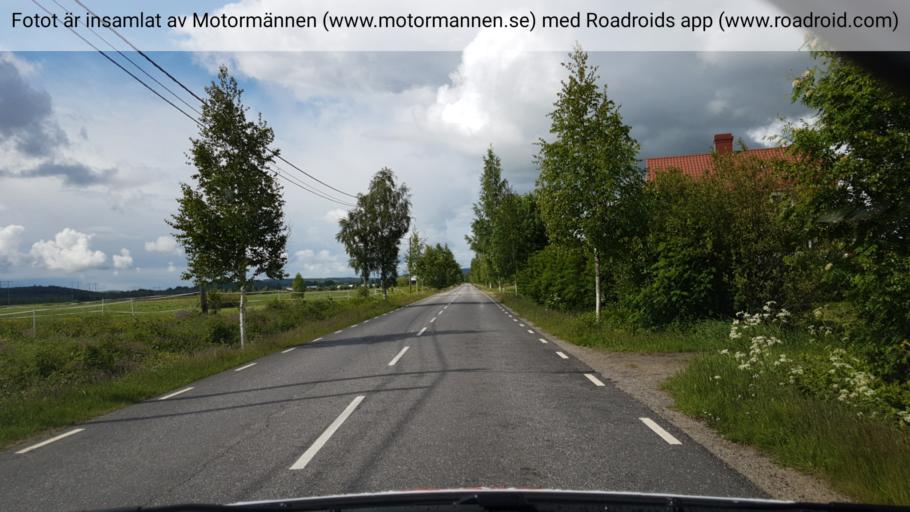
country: SE
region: Vaesterbotten
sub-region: Vannas Kommun
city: Vannasby
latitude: 63.8966
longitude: 19.8783
